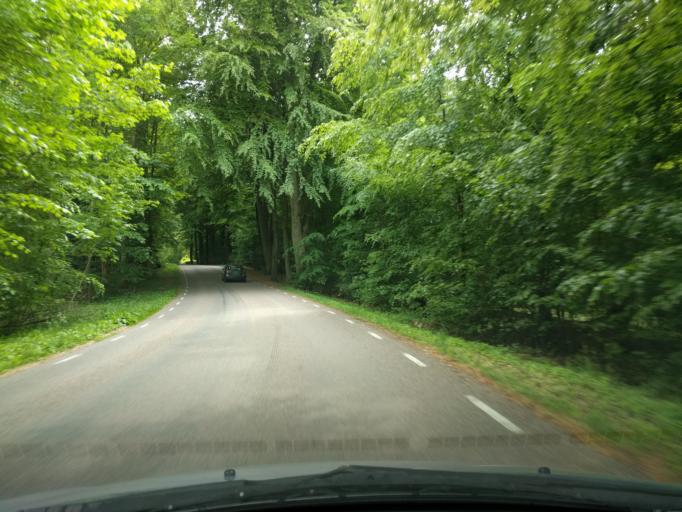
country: SE
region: Skane
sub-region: Svedala Kommun
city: Svedala
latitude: 55.5525
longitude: 13.2071
